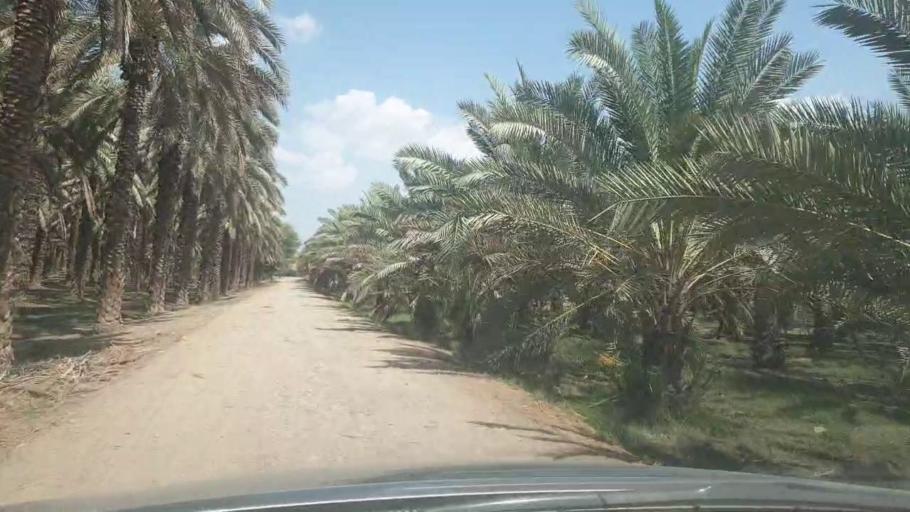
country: PK
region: Sindh
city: Khairpur
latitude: 27.5500
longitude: 68.7936
